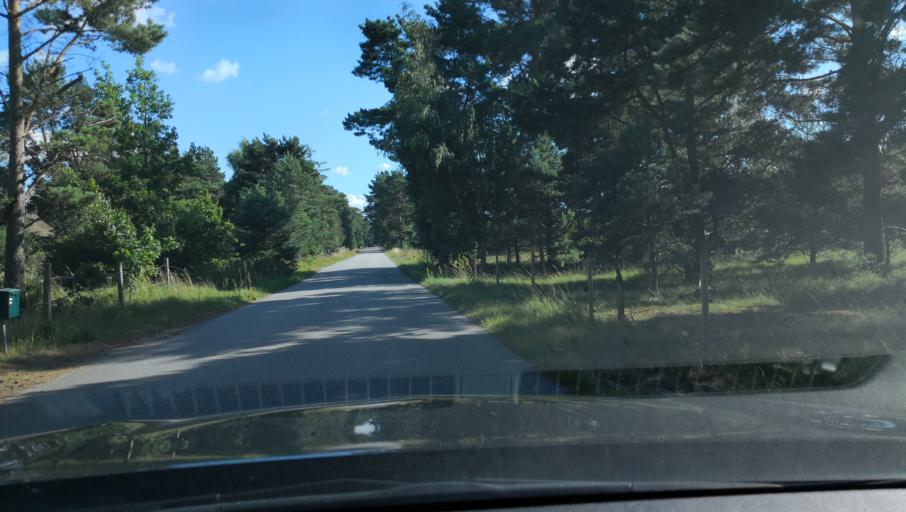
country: SE
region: Skane
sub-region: Simrishamns Kommun
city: Kivik
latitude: 55.7737
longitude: 14.1968
